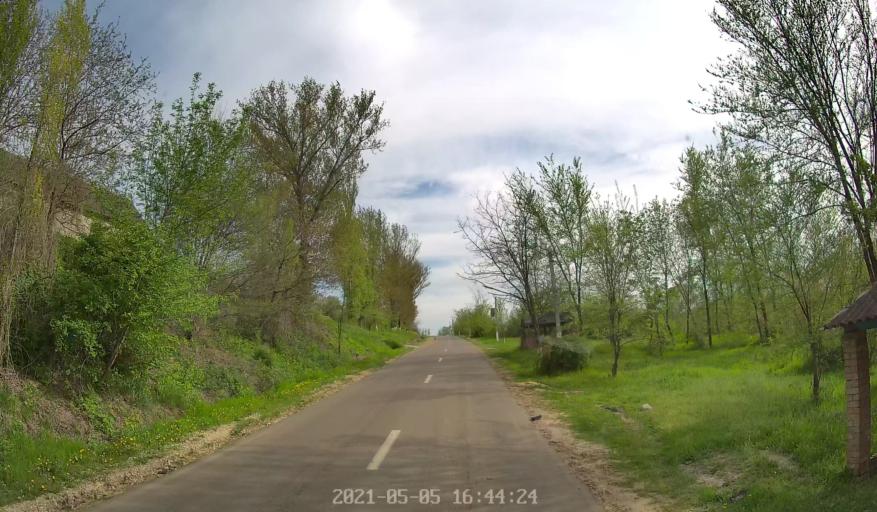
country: MD
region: Criuleni
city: Criuleni
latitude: 47.1176
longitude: 29.1942
